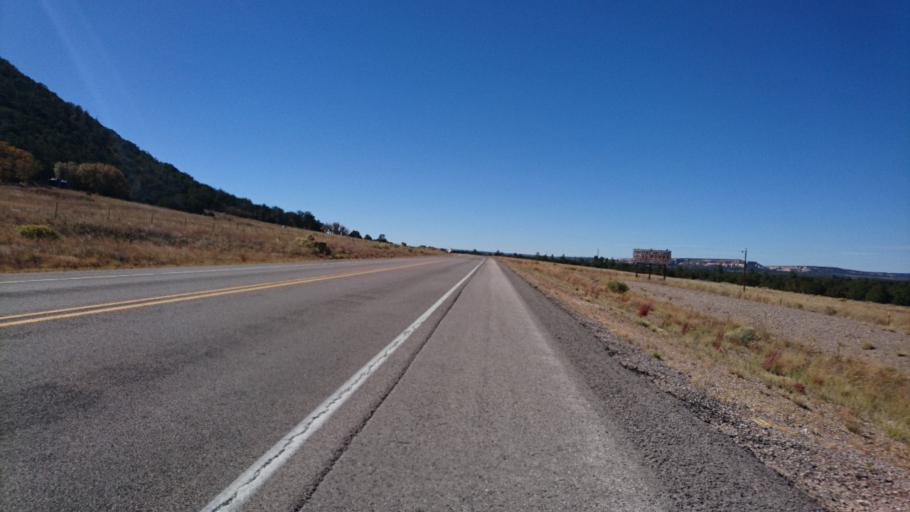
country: US
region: New Mexico
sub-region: McKinley County
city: Thoreau
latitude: 35.0452
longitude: -108.3113
